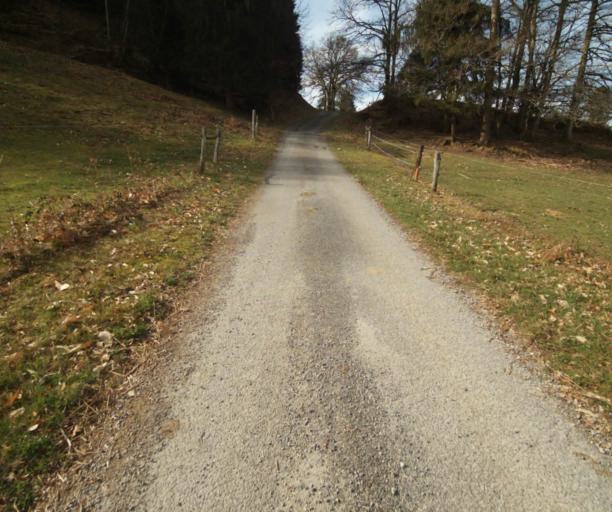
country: FR
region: Limousin
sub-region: Departement de la Correze
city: Correze
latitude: 45.3448
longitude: 1.8636
